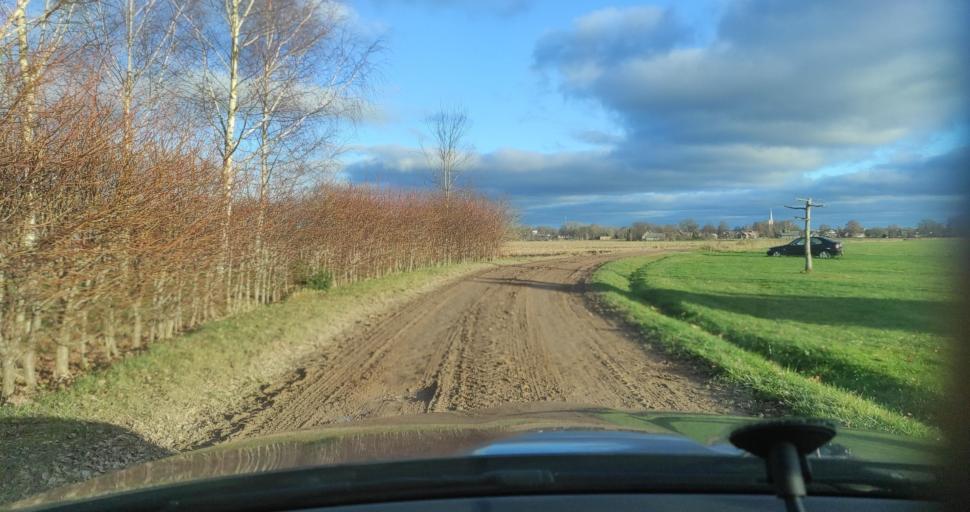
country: LV
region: Kuldigas Rajons
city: Kuldiga
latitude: 57.2708
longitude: 22.0194
